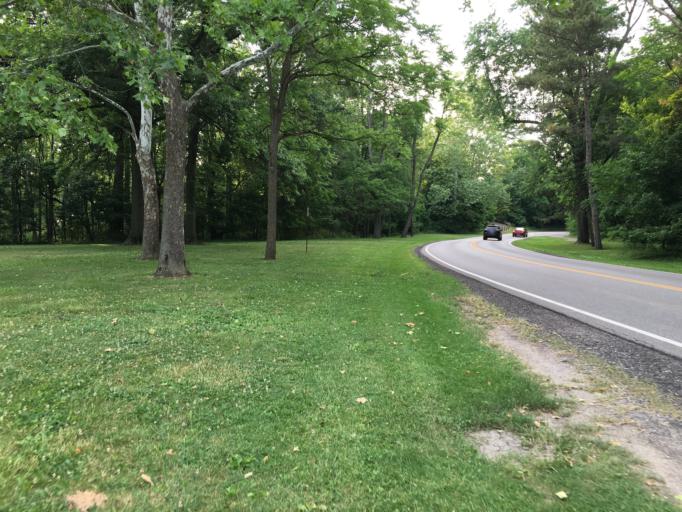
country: US
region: Ohio
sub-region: Cuyahoga County
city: Berea
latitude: 41.3645
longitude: -81.8568
